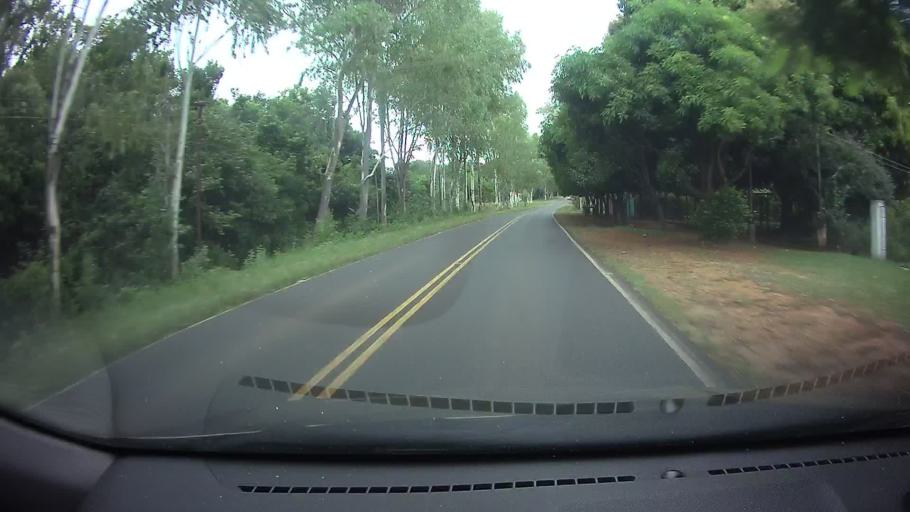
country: PY
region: Central
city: Nueva Italia
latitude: -25.5486
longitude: -57.5000
